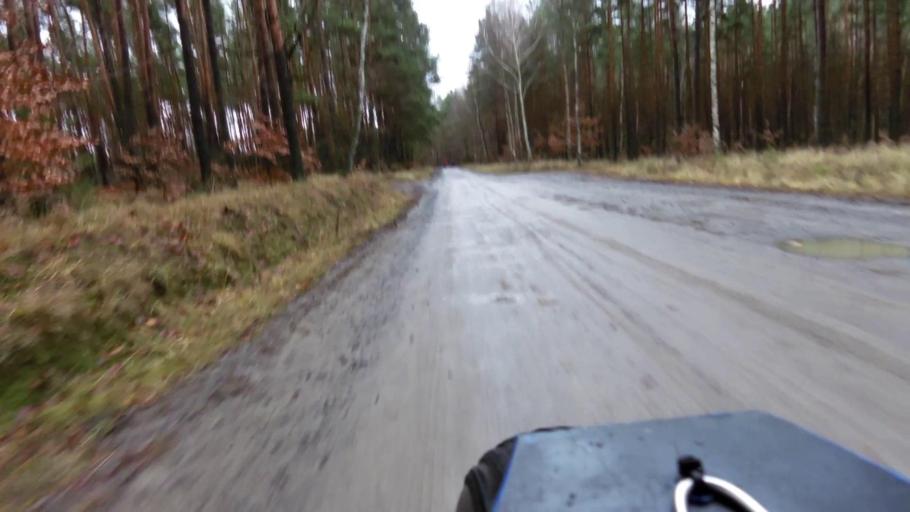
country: PL
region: Lubusz
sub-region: Powiat gorzowski
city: Witnica
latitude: 52.6953
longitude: 14.8466
